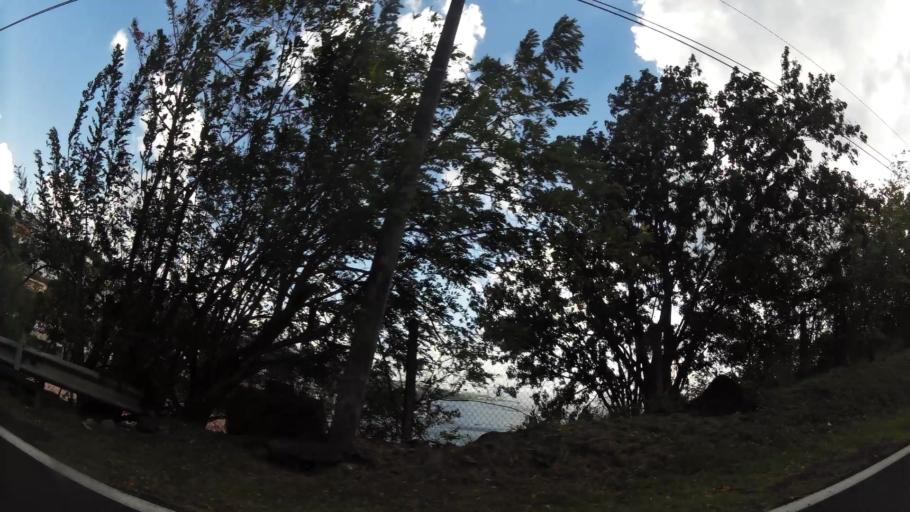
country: MQ
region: Martinique
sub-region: Martinique
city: Fort-de-France
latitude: 14.6283
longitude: -61.1164
